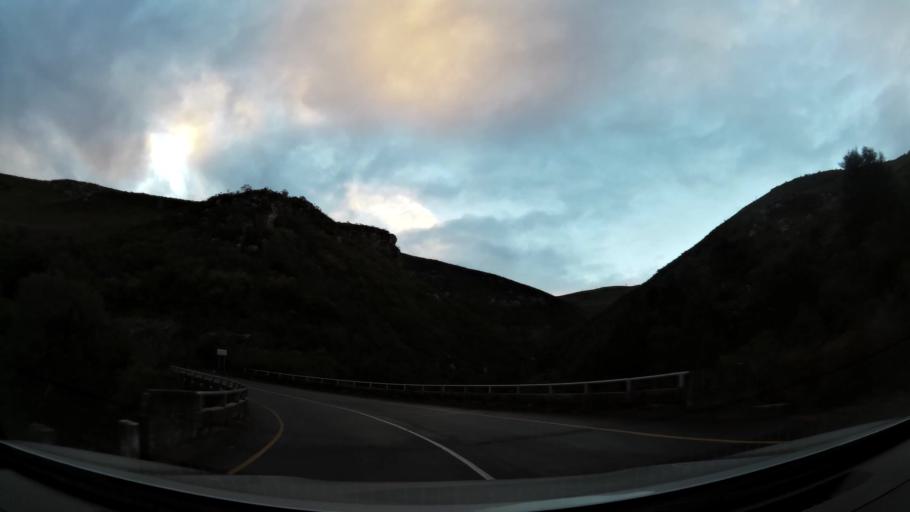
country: ZA
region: Western Cape
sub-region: Overberg District Municipality
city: Swellendam
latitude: -33.9854
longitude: 20.7195
